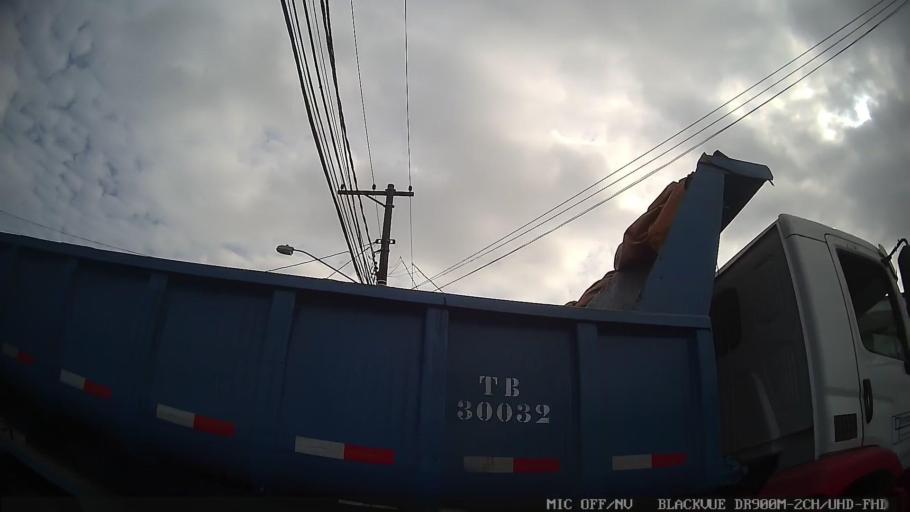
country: BR
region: Sao Paulo
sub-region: Guaruja
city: Guaruja
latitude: -23.9599
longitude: -46.2846
